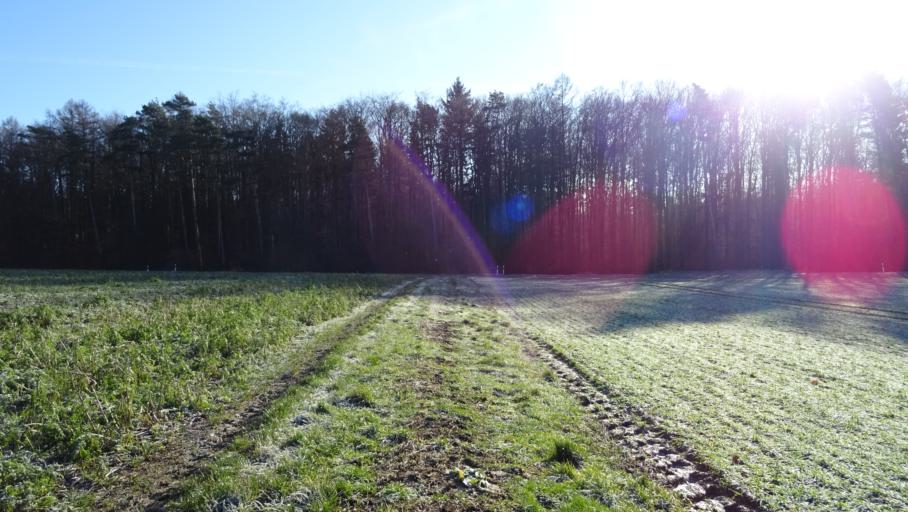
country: DE
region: Baden-Wuerttemberg
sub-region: Karlsruhe Region
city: Mosbach
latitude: 49.3409
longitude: 9.1901
